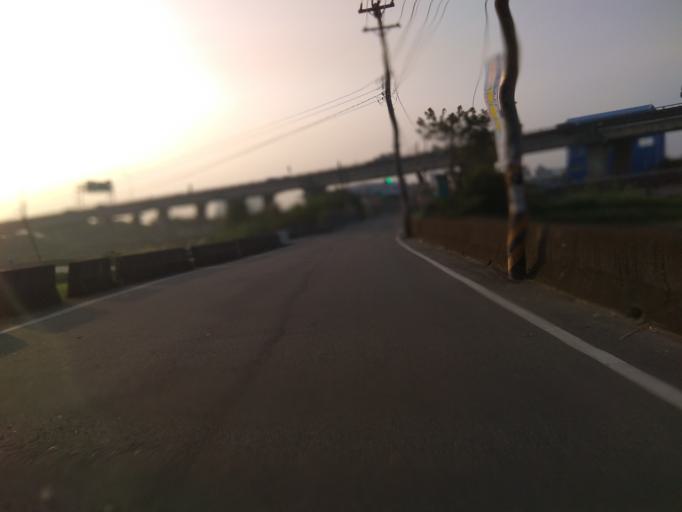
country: TW
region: Taiwan
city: Daxi
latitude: 24.9296
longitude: 121.2055
